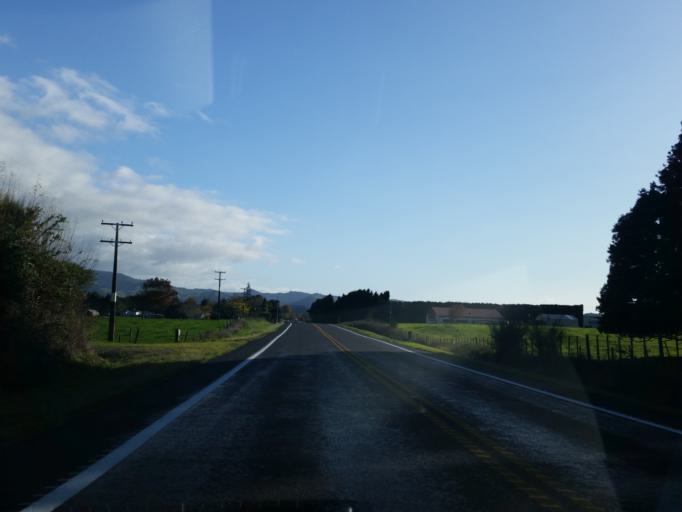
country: NZ
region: Waikato
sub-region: Hauraki District
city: Waihi
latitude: -37.4316
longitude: 175.8719
